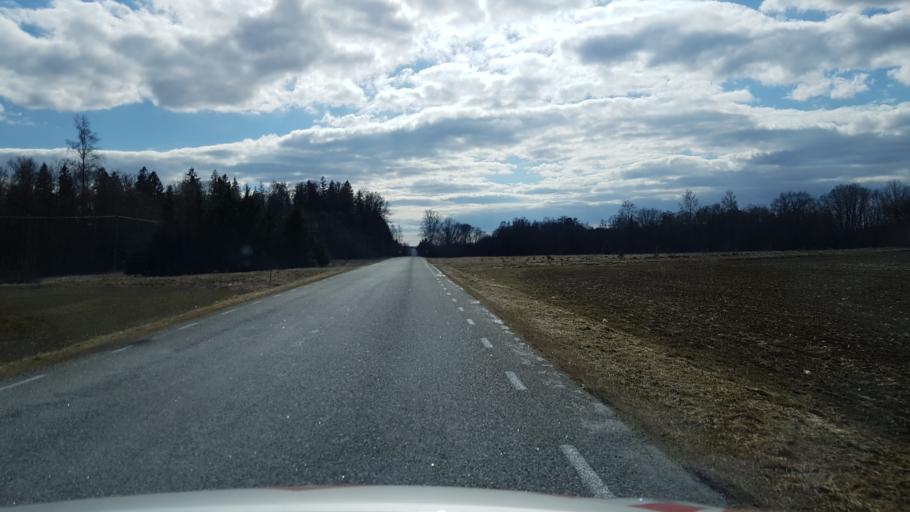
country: EE
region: Laeaene-Virumaa
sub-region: Kadrina vald
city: Kadrina
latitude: 59.3098
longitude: 26.2336
